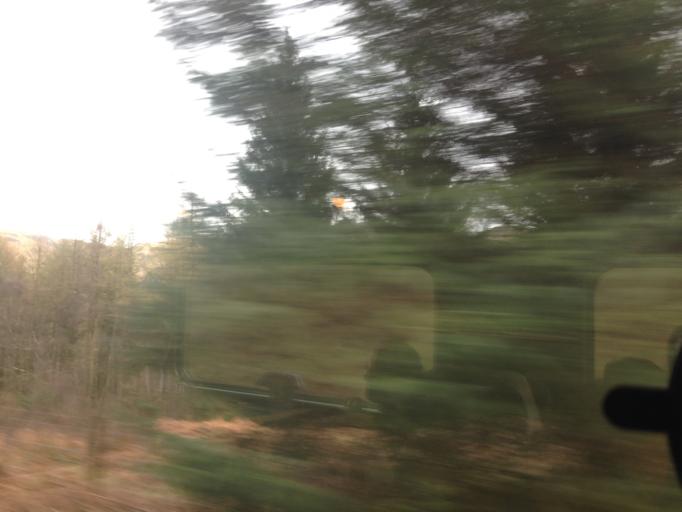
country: GB
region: Scotland
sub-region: Argyll and Bute
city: Garelochhead
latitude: 56.2129
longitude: -4.7014
